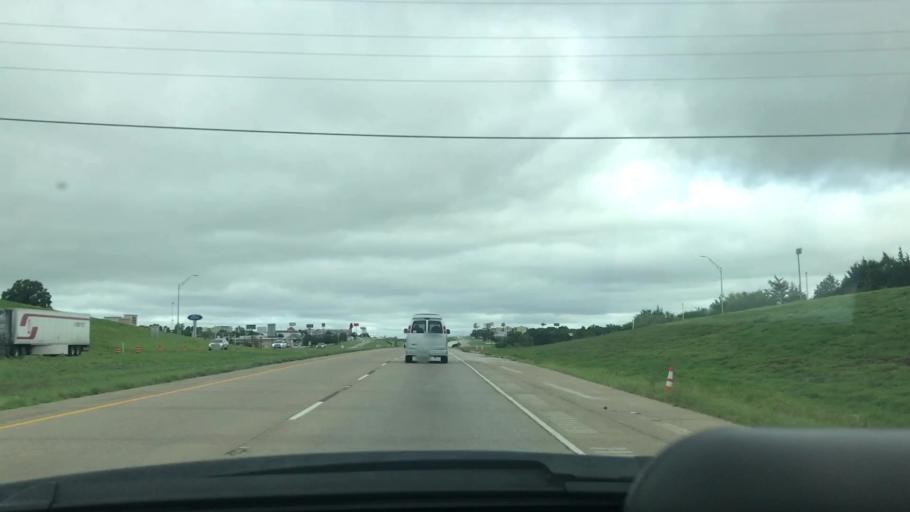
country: US
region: Texas
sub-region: Grayson County
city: Denison
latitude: 33.7522
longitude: -96.5852
